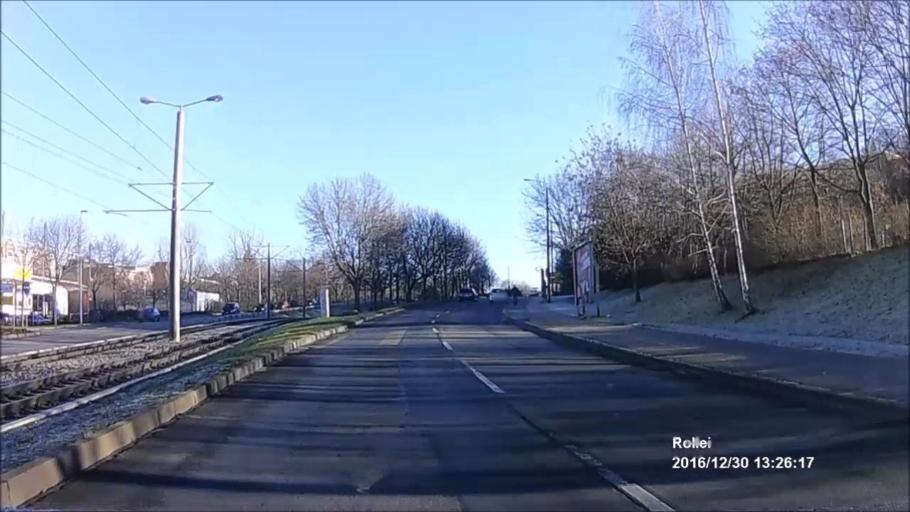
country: DE
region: Thuringia
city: Erfurt
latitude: 50.9549
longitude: 11.0678
